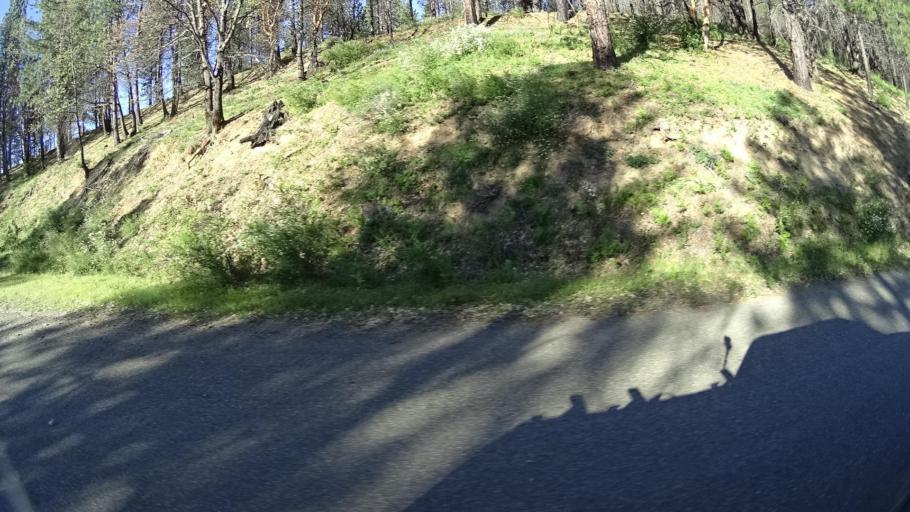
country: US
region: California
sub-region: Lake County
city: Upper Lake
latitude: 39.3132
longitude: -122.9460
